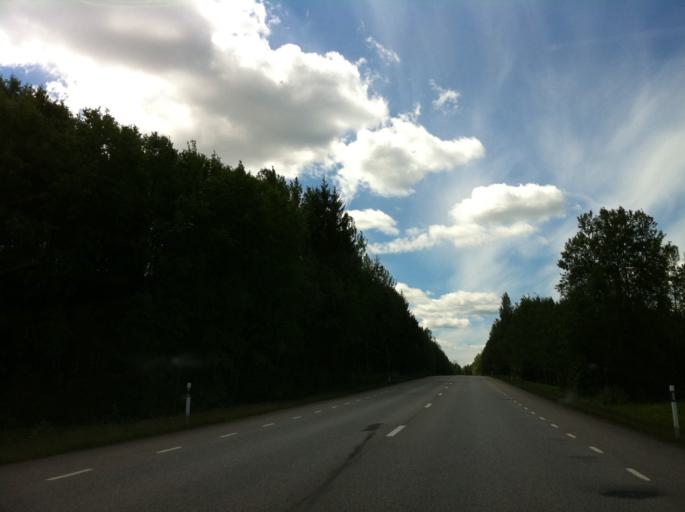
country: SE
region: Vaestra Goetaland
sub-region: Amals Kommun
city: Amal
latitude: 59.0001
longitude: 12.6823
